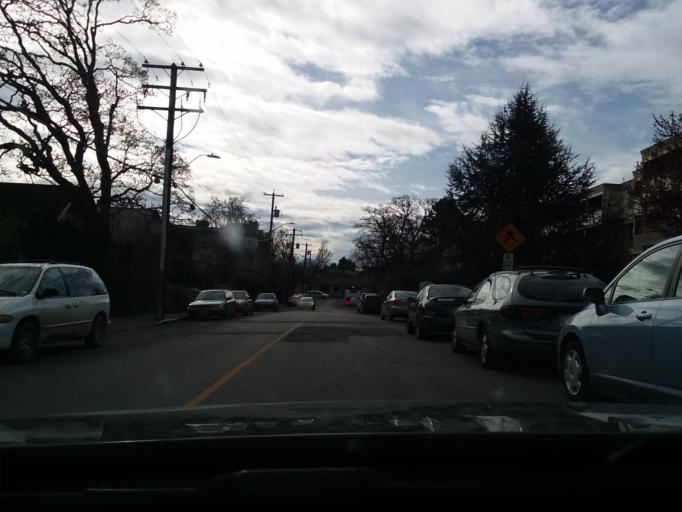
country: CA
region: British Columbia
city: Victoria
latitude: 48.4293
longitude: -123.3347
